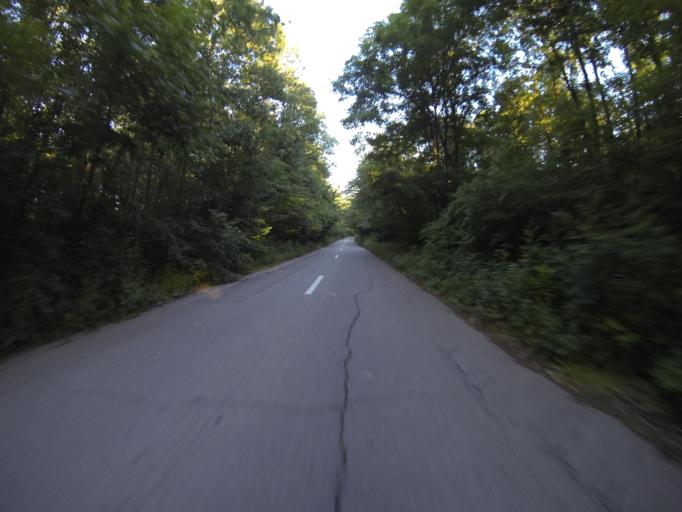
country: RO
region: Dolj
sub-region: Comuna Tuglui
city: Tuglui
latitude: 44.1692
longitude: 23.8241
